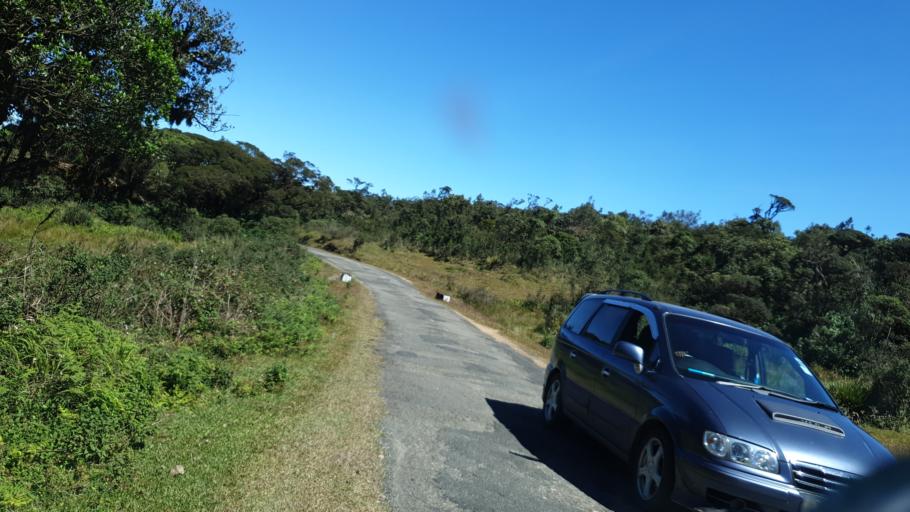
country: LK
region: Central
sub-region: Nuwara Eliya District
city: Nuwara Eliya
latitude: 6.8372
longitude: 80.8108
